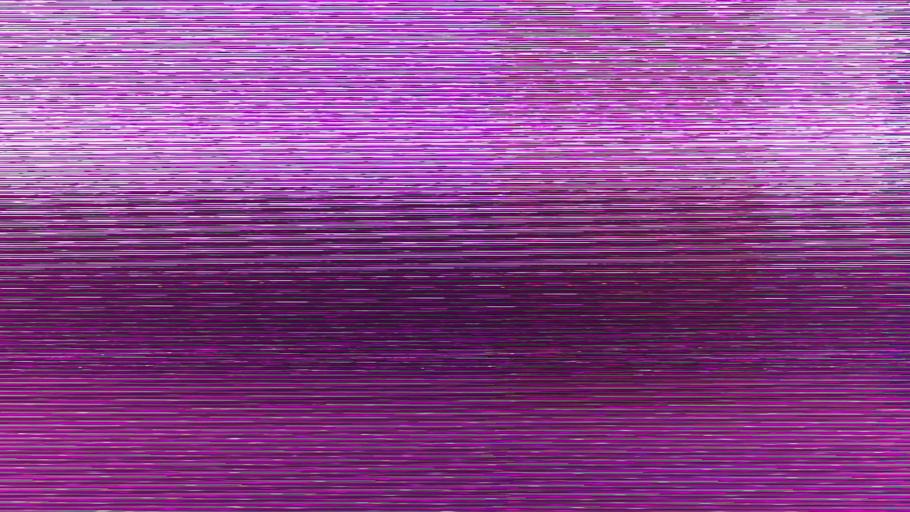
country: US
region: Michigan
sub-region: Washtenaw County
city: Ypsilanti
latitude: 42.2027
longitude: -83.6100
